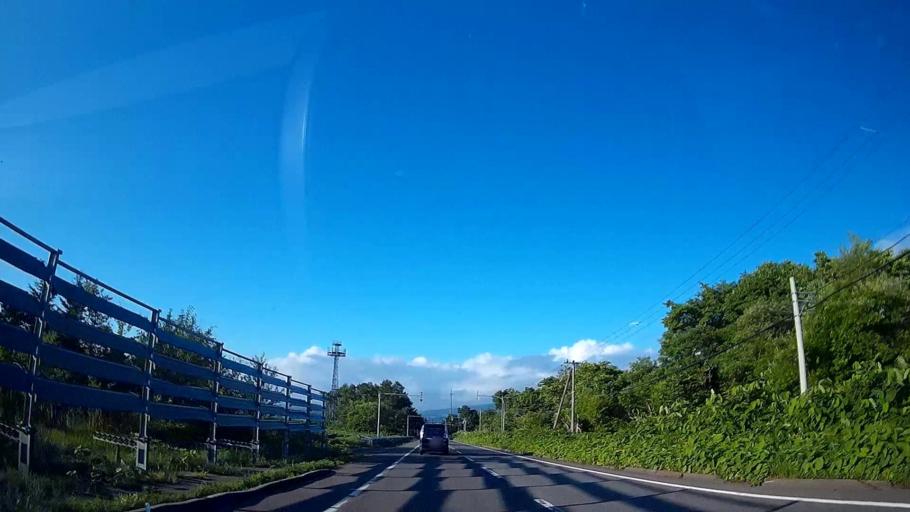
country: JP
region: Hokkaido
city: Date
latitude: 42.6219
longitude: 140.7947
